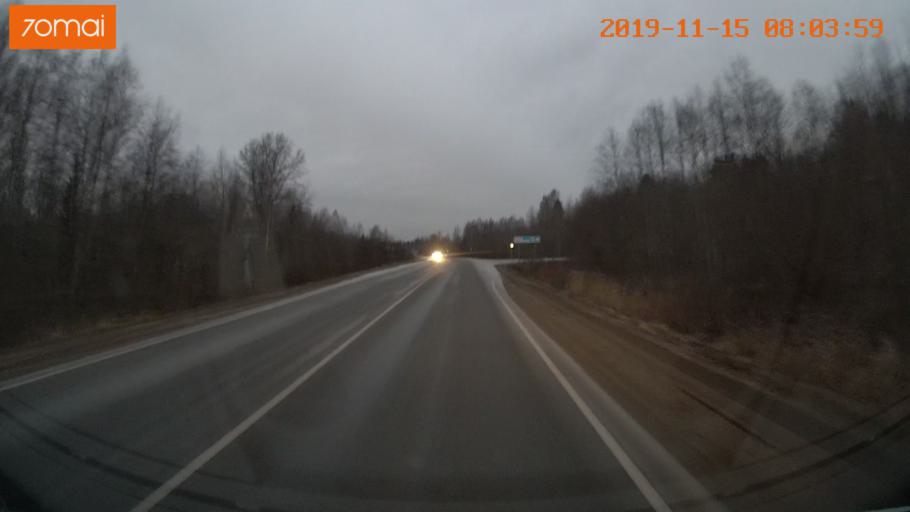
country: RU
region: Vologda
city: Cherepovets
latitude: 59.0036
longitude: 38.0827
